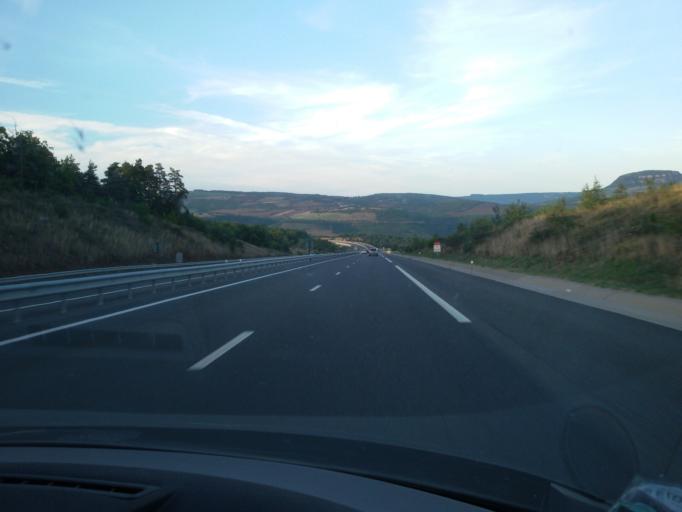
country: FR
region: Midi-Pyrenees
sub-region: Departement de l'Aveyron
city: Millau
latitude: 44.1886
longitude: 3.0563
